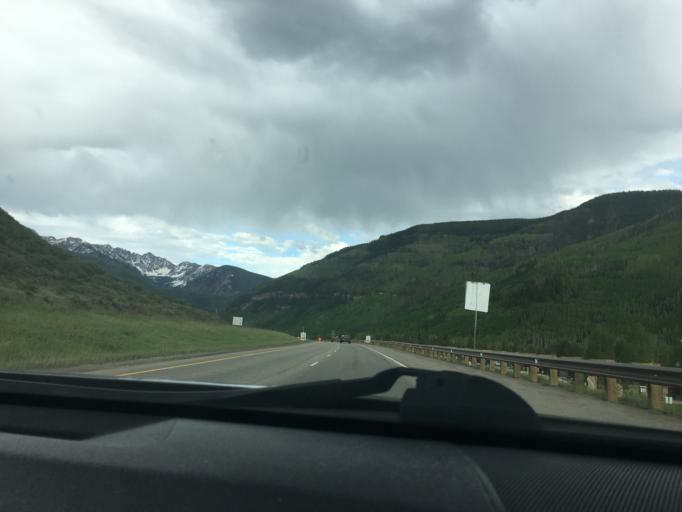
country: US
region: Colorado
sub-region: Eagle County
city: Vail
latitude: 39.6414
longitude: -106.3653
